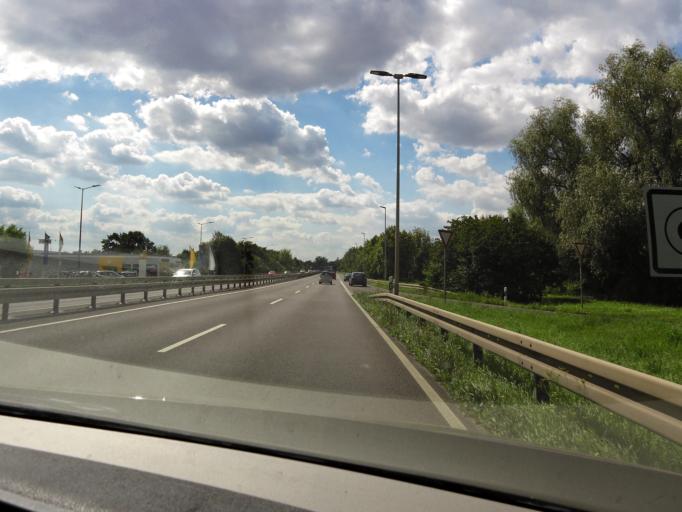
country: DE
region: Saxony-Anhalt
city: Neue Neustadt
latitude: 52.1504
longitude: 11.6275
